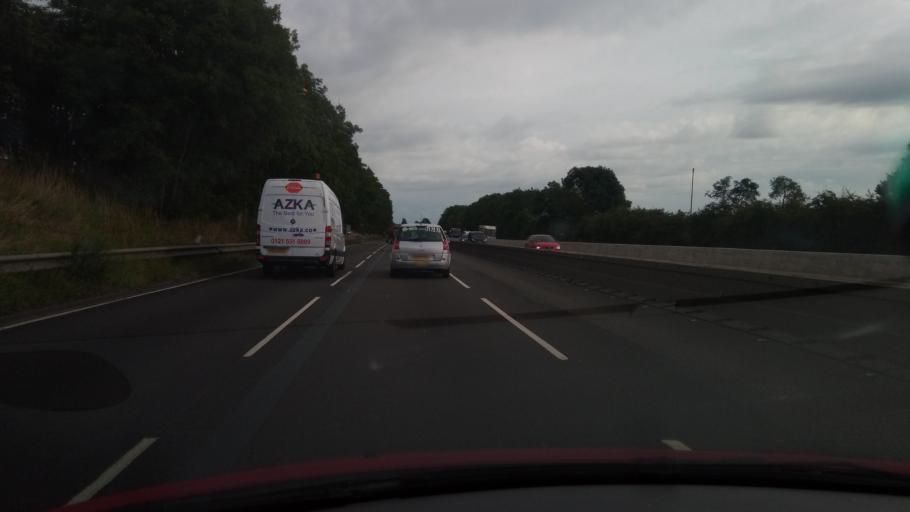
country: GB
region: England
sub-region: Staffordshire
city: Stone
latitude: 52.8552
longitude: -2.1614
